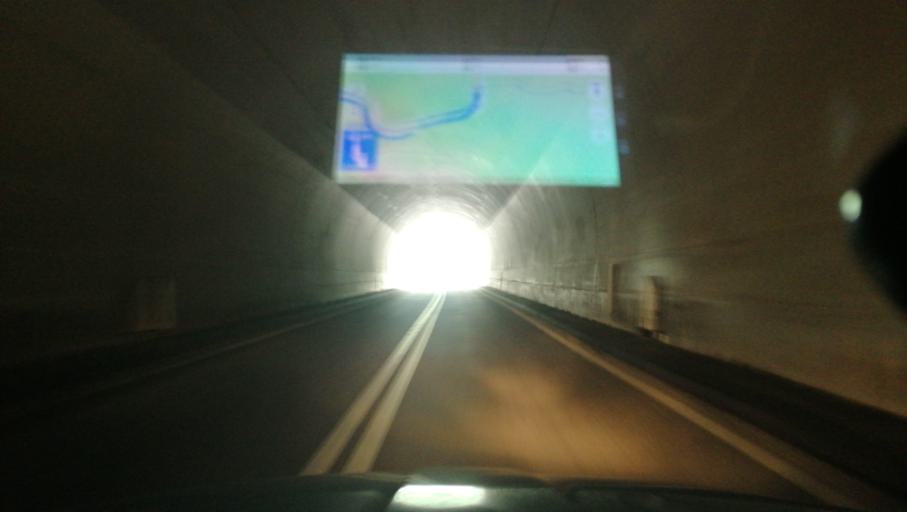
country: BA
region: Federation of Bosnia and Herzegovina
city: Jajce
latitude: 44.4549
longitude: 17.2386
